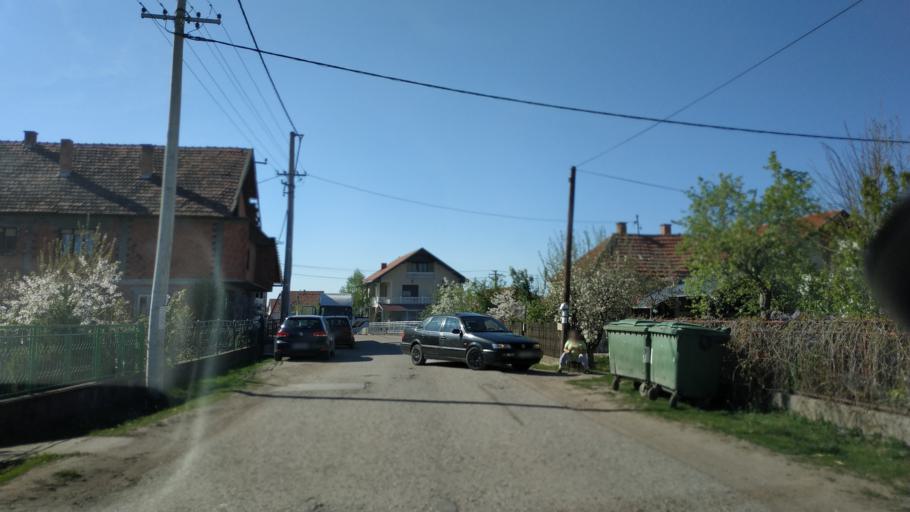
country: RS
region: Central Serbia
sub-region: Nisavski Okrug
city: Aleksinac
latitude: 43.5091
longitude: 21.6867
